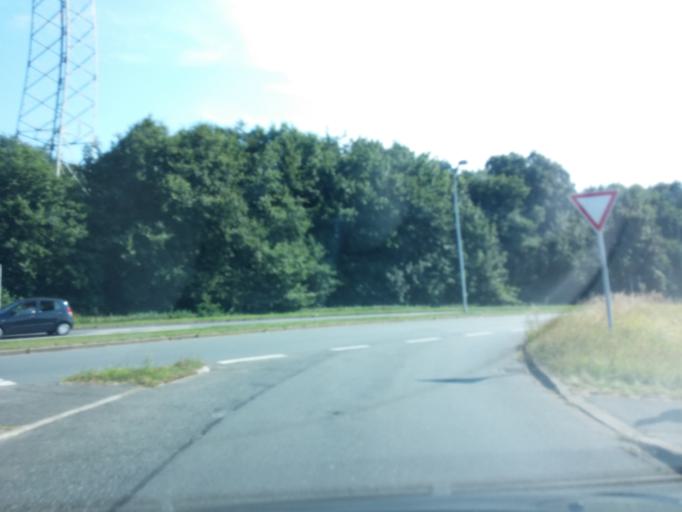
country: DE
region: North Rhine-Westphalia
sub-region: Regierungsbezirk Munster
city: Gladbeck
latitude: 51.6120
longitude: 7.0244
